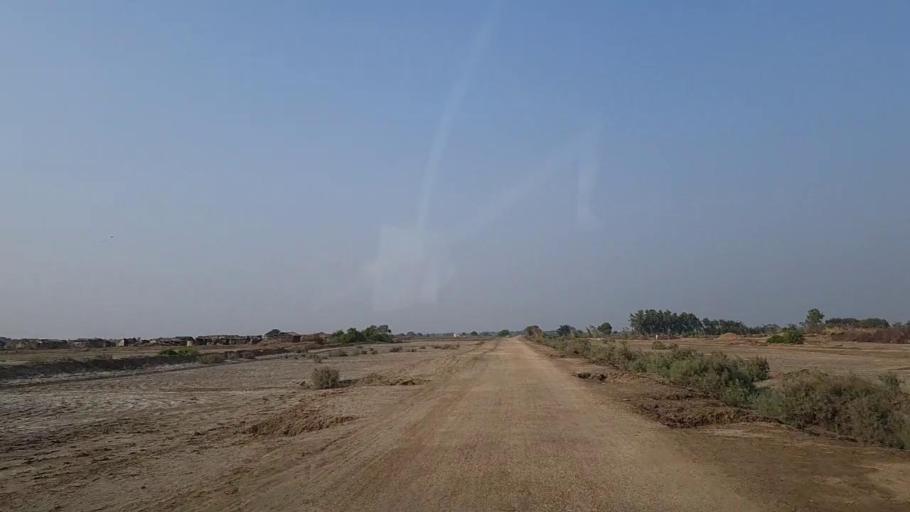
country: PK
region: Sindh
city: Mirpur Sakro
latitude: 24.6300
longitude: 67.7679
